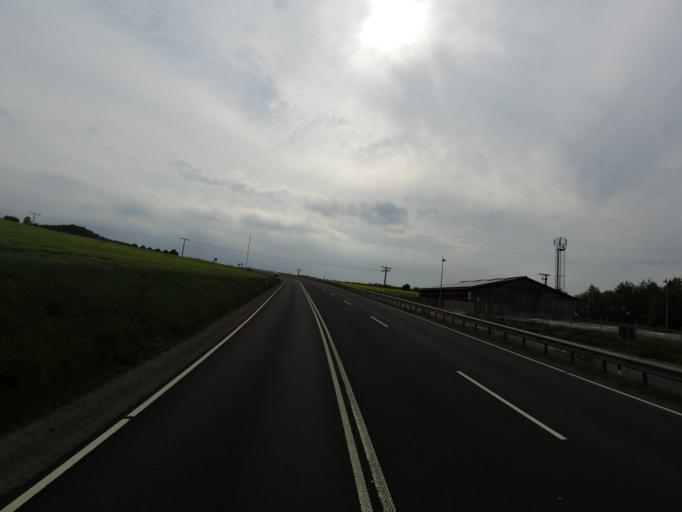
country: DE
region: Rheinland-Pfalz
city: Waldesch
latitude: 50.2742
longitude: 7.5413
